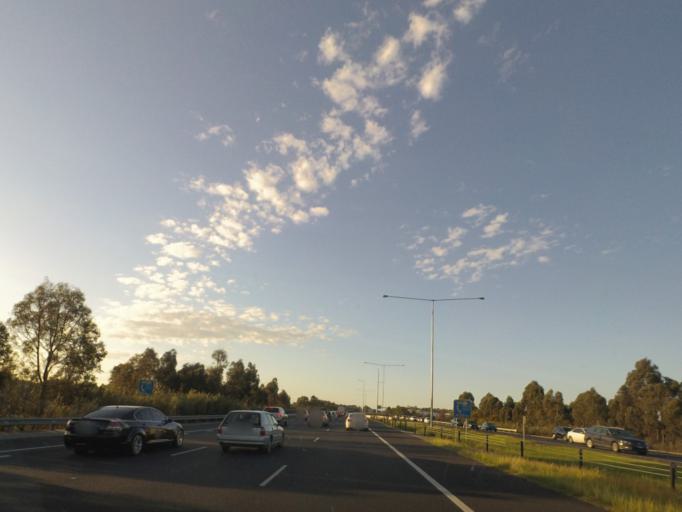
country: AU
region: Victoria
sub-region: Knox
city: Scoresby
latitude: -37.9046
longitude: 145.2155
